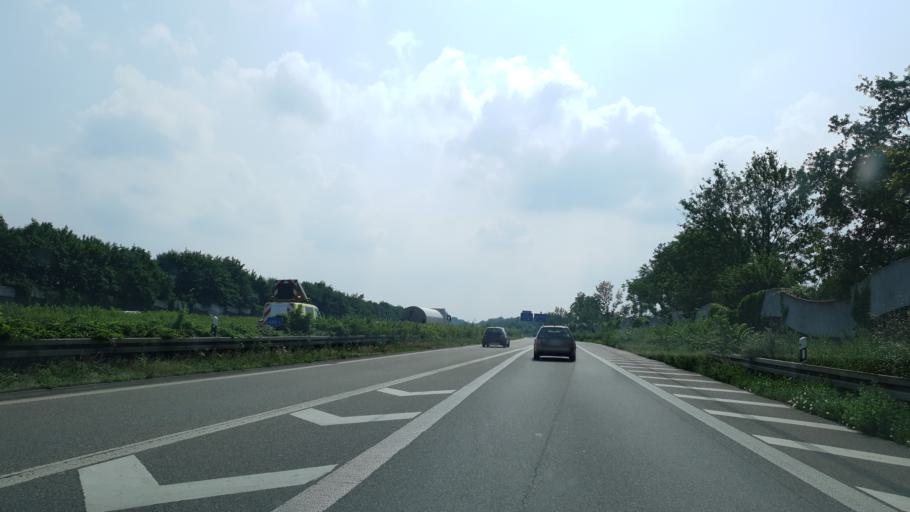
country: DE
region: North Rhine-Westphalia
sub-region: Regierungsbezirk Munster
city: Bottrop
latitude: 51.5537
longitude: 6.9214
